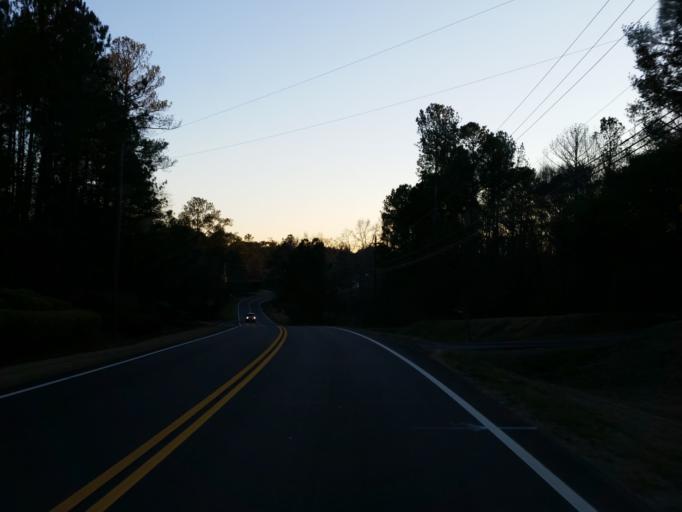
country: US
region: Georgia
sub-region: Cherokee County
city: Woodstock
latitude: 34.0954
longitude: -84.4742
